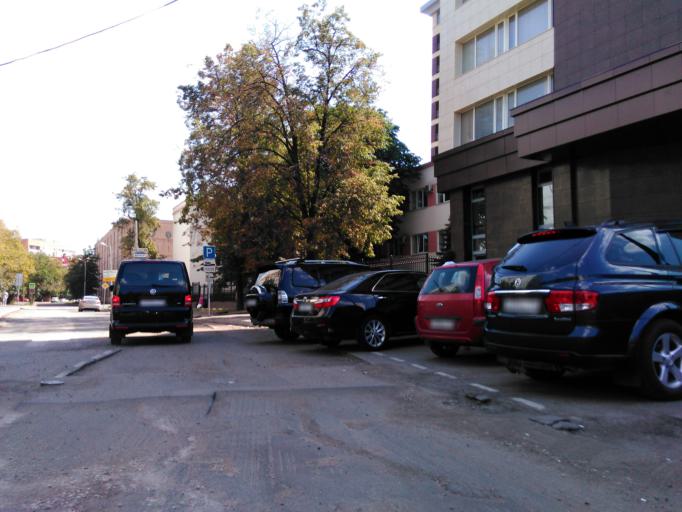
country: RU
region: Moscow
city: Novyye Cheremushki
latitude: 55.7090
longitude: 37.5980
